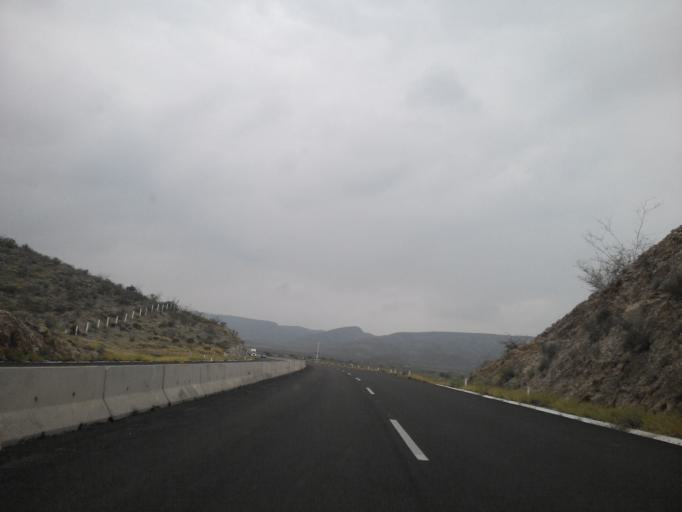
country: MX
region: Durango
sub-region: Lerdo
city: Sapioris
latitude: 25.3692
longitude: -103.6677
